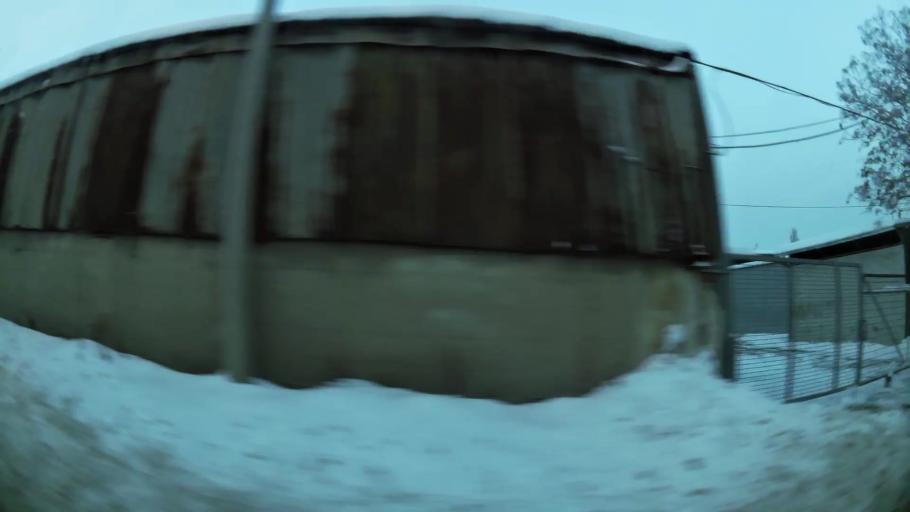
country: RS
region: Central Serbia
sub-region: Belgrade
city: Stari Grad
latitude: 44.8214
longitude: 20.4887
